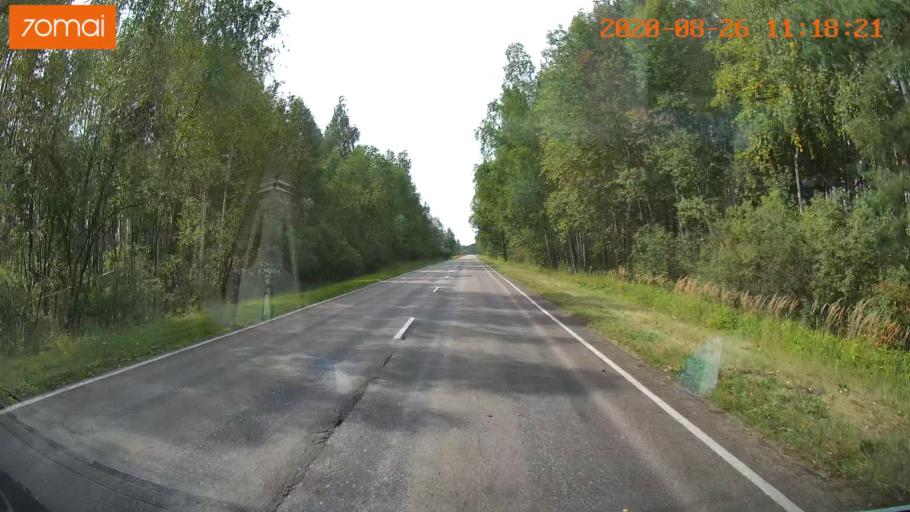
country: RU
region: Rjazan
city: Shilovo
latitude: 54.4108
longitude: 41.0986
